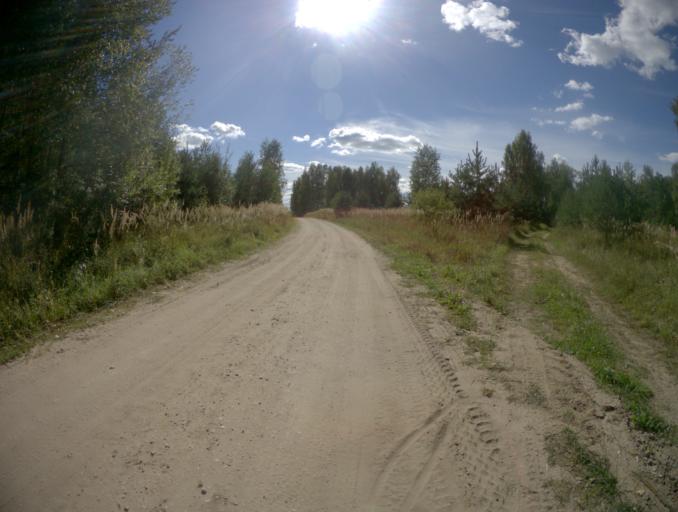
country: RU
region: Vladimir
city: Krasnaya Gorbatka
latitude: 55.8608
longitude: 41.7962
